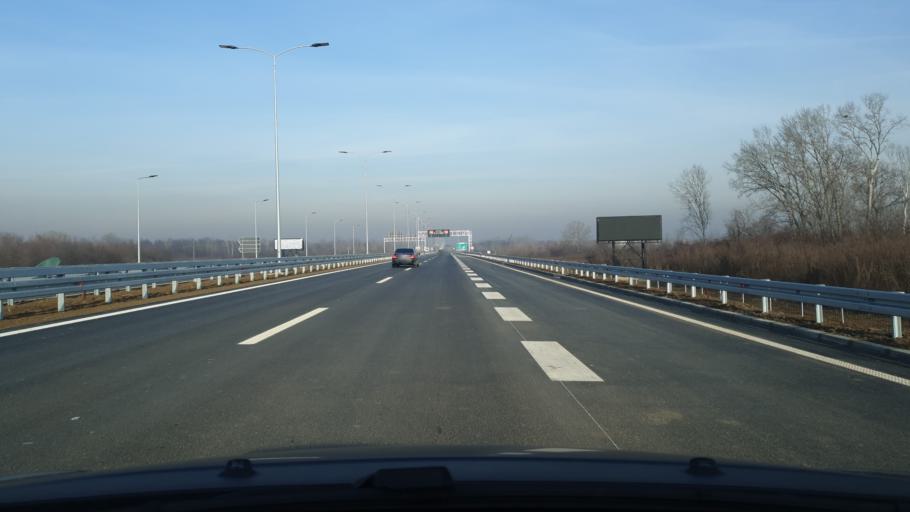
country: RS
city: Baric
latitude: 44.6538
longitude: 20.2337
